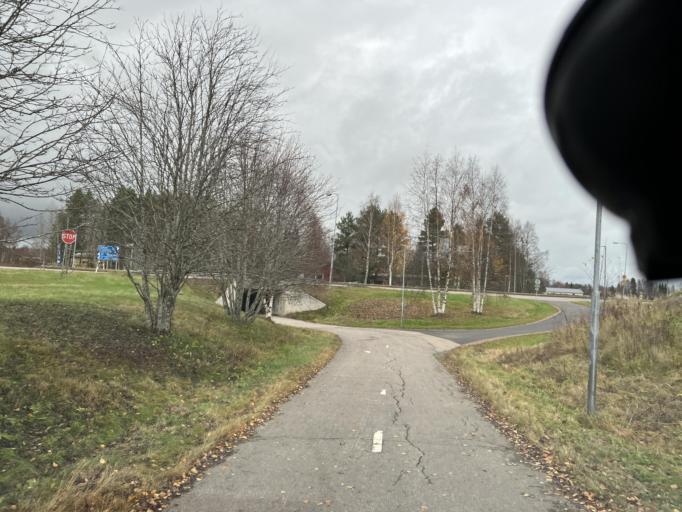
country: FI
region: Northern Ostrobothnia
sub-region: Ylivieska
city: Ylivieska
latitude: 64.0751
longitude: 24.4661
